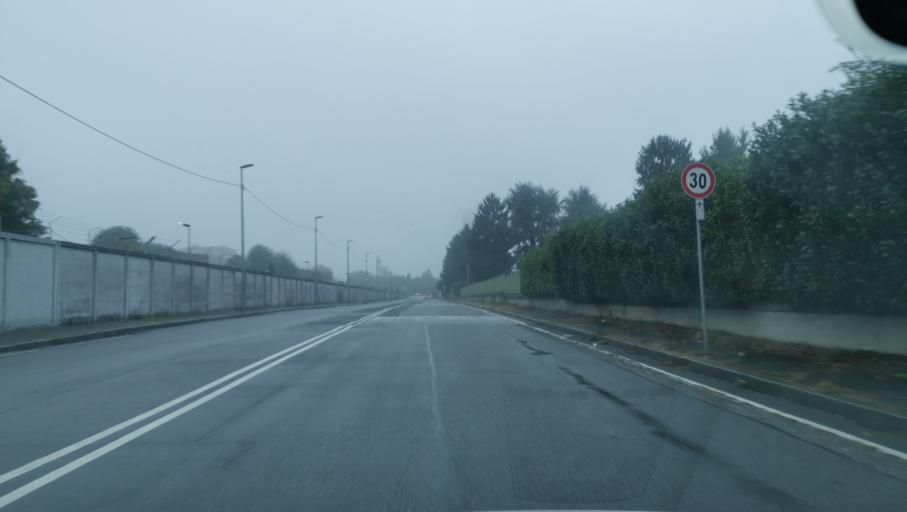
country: IT
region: Piedmont
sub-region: Provincia di Torino
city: Turin
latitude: 45.1145
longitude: 7.7147
